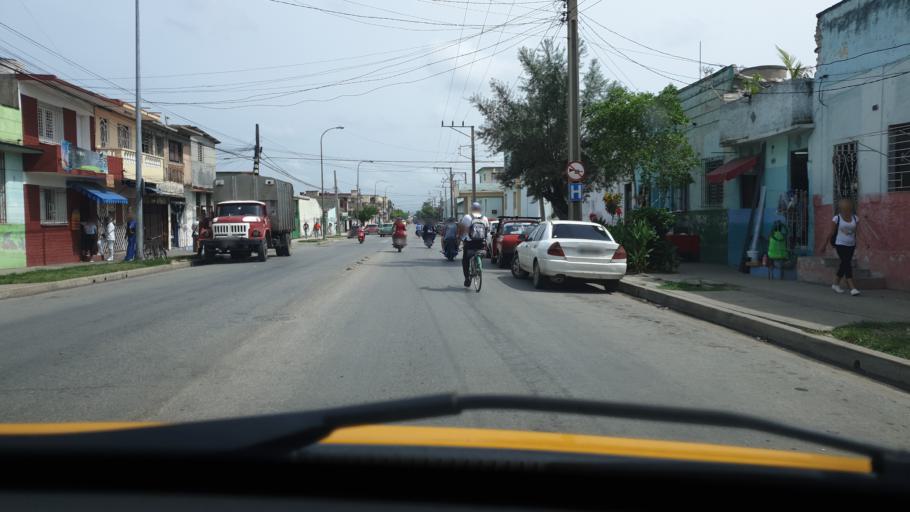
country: CU
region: Villa Clara
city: Santa Clara
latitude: 22.3953
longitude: -79.9622
